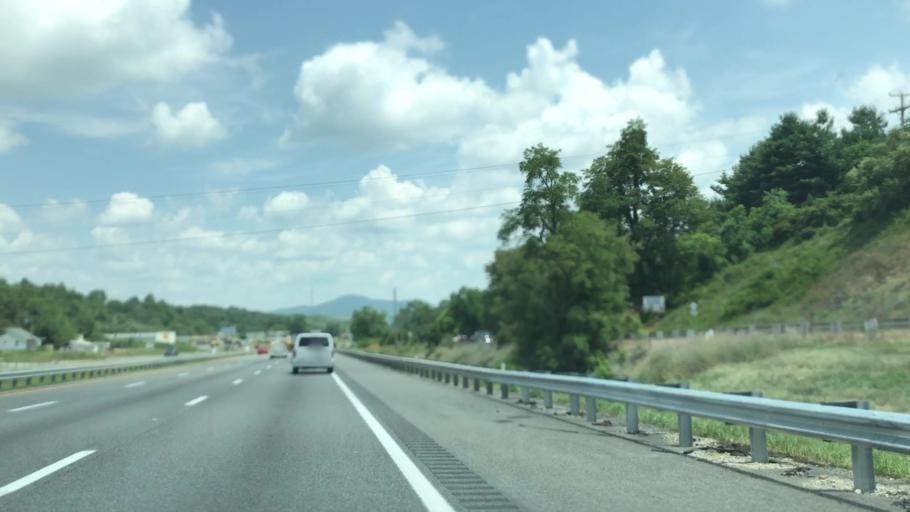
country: US
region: Virginia
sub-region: Wythe County
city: Wytheville
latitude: 36.9404
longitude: -80.9748
